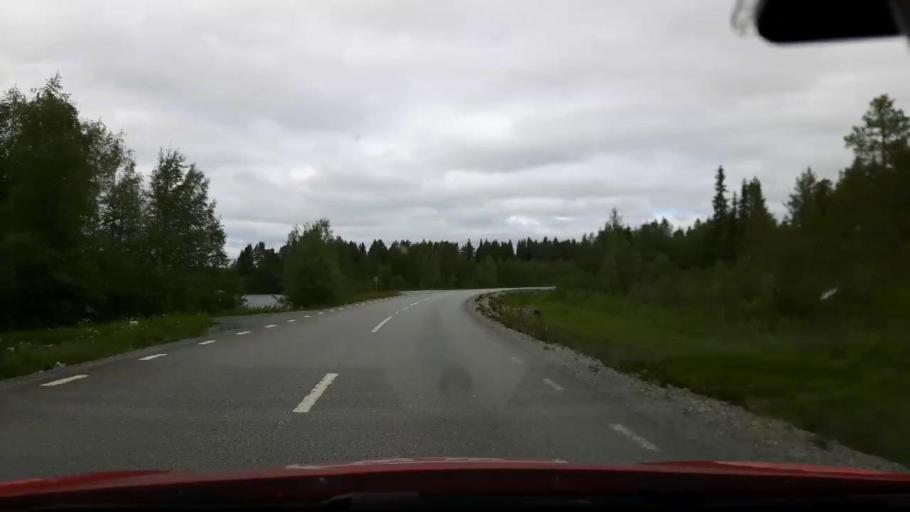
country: SE
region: Jaemtland
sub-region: OEstersunds Kommun
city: Lit
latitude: 63.6831
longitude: 14.6739
